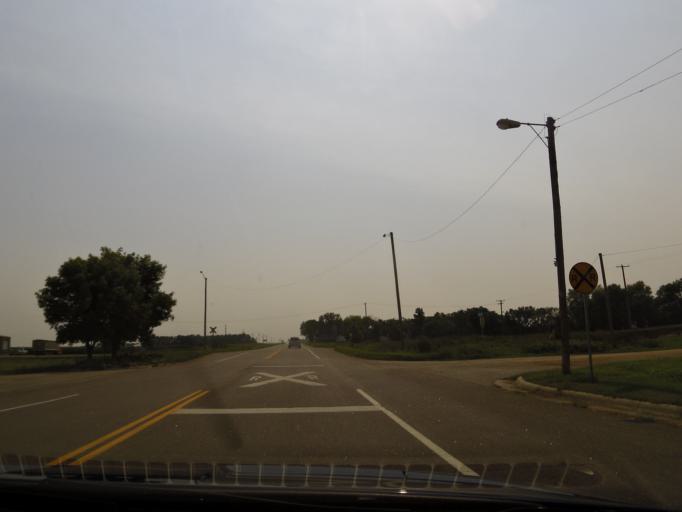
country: US
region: South Dakota
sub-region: Roberts County
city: Sisseton
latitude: 45.8561
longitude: -97.1038
